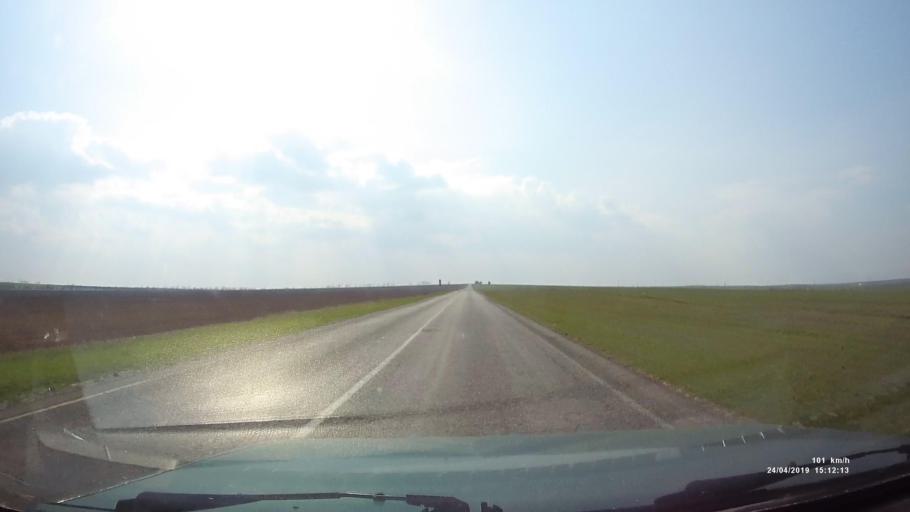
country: RU
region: Rostov
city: Remontnoye
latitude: 46.5464
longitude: 43.3053
